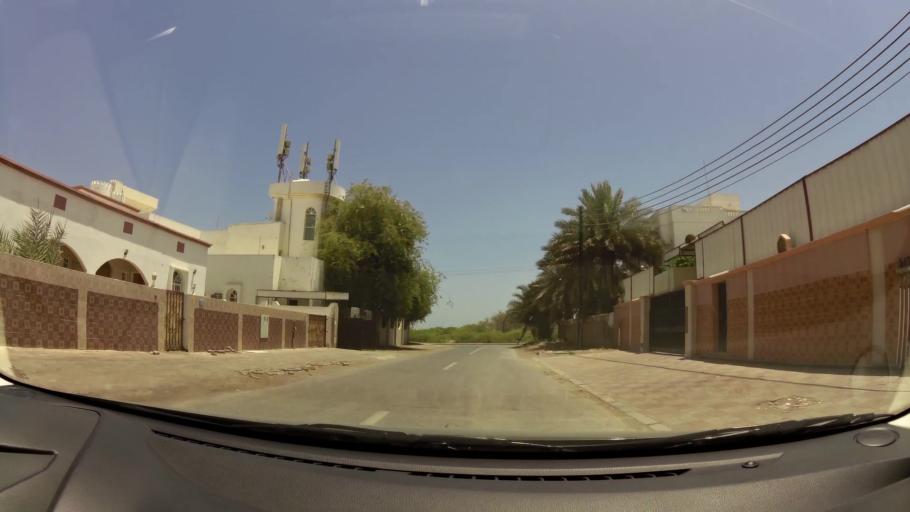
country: OM
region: Muhafazat Masqat
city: As Sib al Jadidah
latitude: 23.6340
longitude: 58.2437
